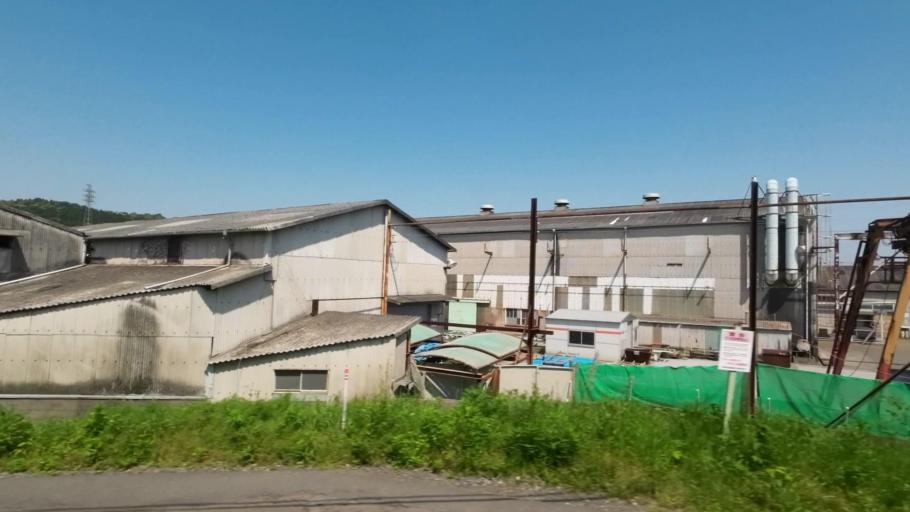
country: JP
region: Ehime
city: Niihama
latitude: 33.9415
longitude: 133.2873
